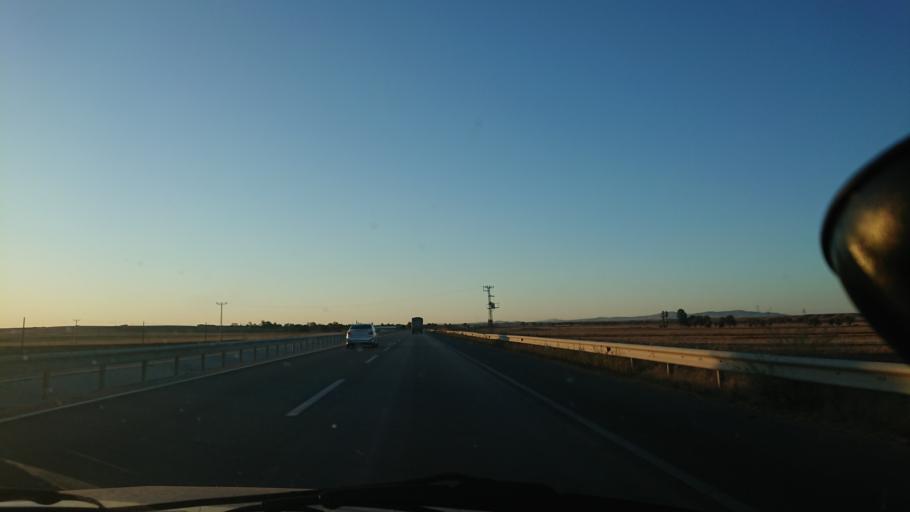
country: TR
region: Eskisehir
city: Mahmudiye
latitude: 39.5282
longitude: 30.9518
